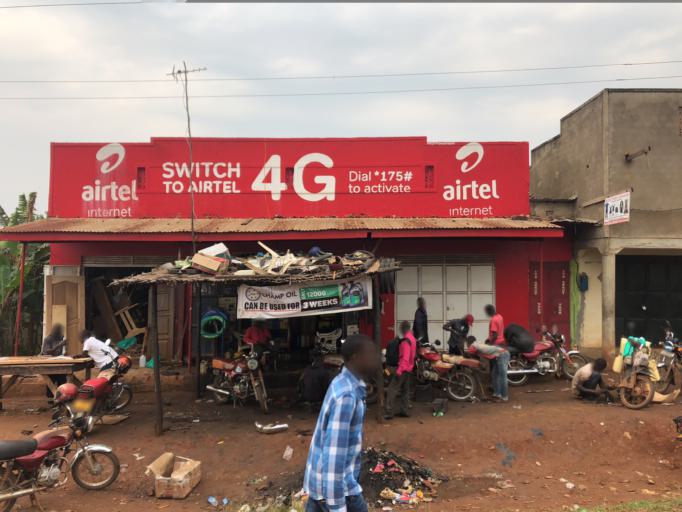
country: UG
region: Central Region
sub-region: Mukono District
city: Mukono
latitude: 0.3471
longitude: 32.7635
